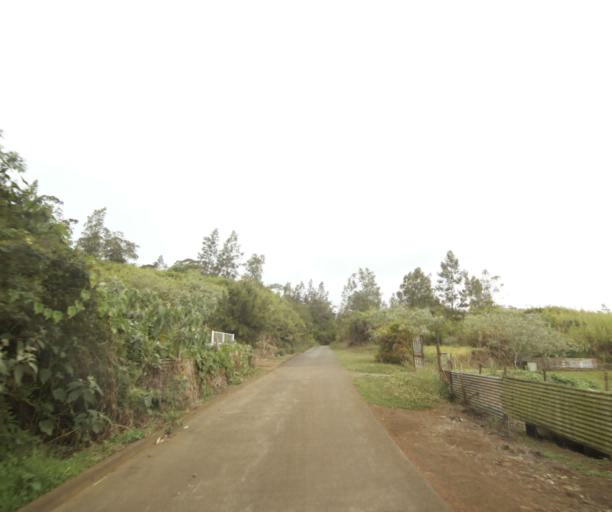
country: RE
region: Reunion
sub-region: Reunion
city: Saint-Paul
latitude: -21.0144
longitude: 55.3539
